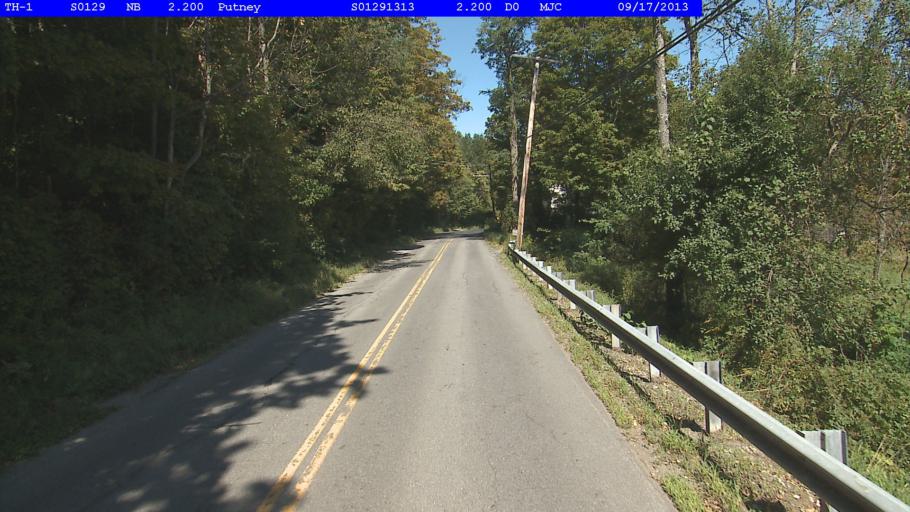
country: US
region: New Hampshire
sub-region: Cheshire County
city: Westmoreland
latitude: 43.0042
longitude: -72.5321
